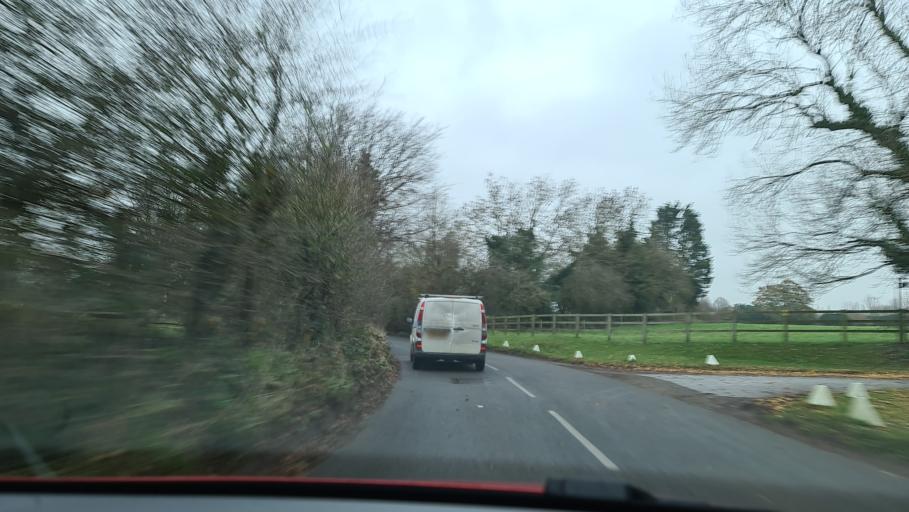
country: GB
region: England
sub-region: Buckinghamshire
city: Seer Green
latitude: 51.6205
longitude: -0.5899
